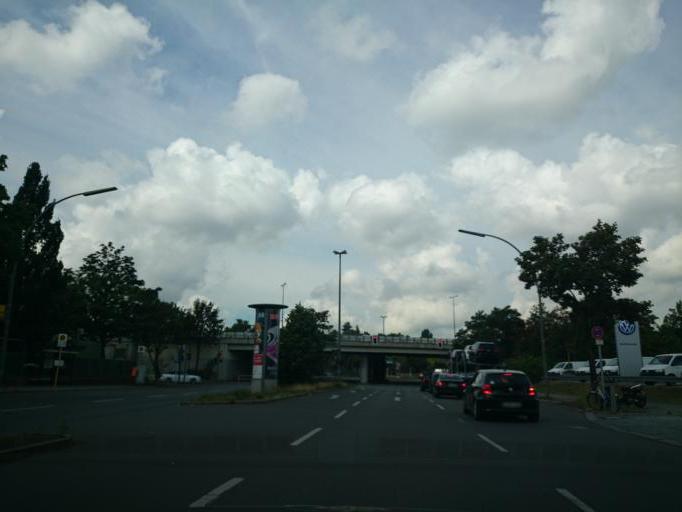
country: DE
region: Berlin
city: Tempelhof Bezirk
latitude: 52.4637
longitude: 13.4050
